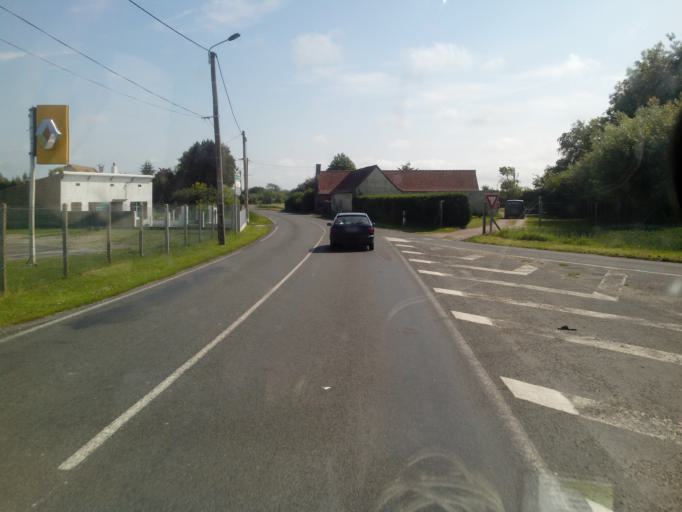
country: FR
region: Picardie
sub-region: Departement de la Somme
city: Quend
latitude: 50.3130
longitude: 1.6384
